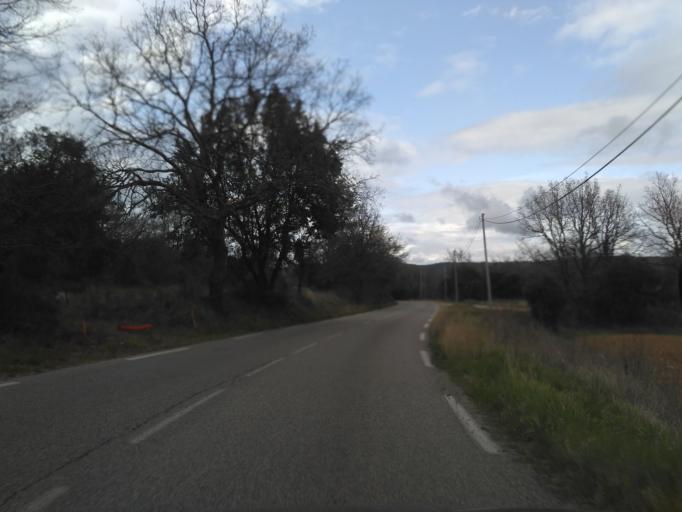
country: FR
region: Provence-Alpes-Cote d'Azur
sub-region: Departement du Var
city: Barjols
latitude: 43.5758
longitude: 6.0164
